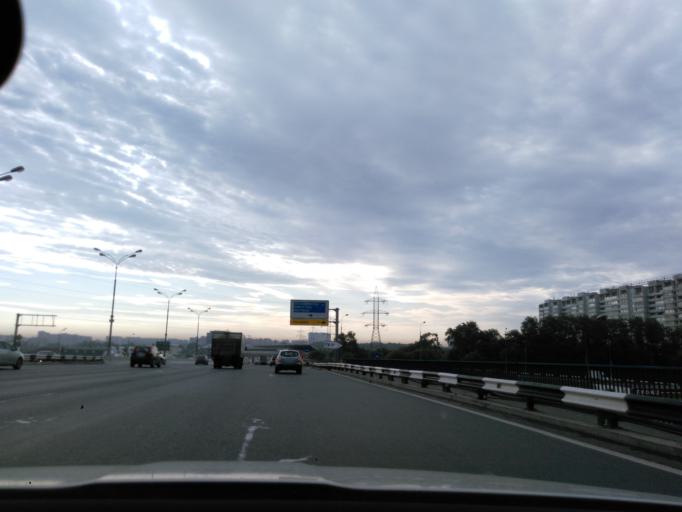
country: RU
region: Moscow
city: Vatutino
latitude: 55.8950
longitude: 37.6731
